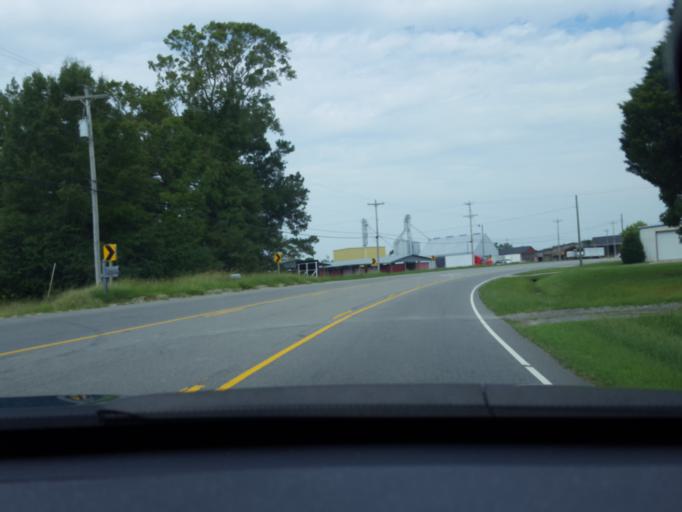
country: US
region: North Carolina
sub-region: Chowan County
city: Edenton
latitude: 36.0848
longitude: -76.6293
